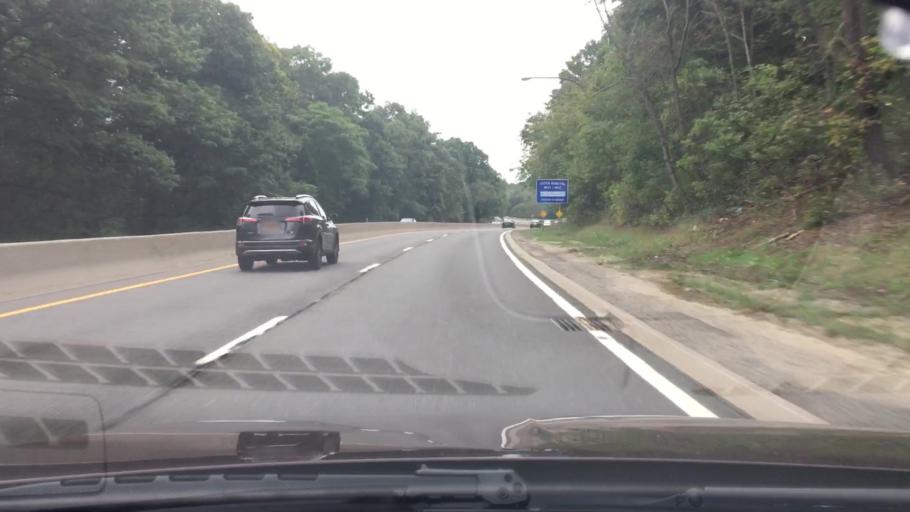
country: US
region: New York
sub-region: Suffolk County
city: West Hills
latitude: 40.8044
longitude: -73.4475
